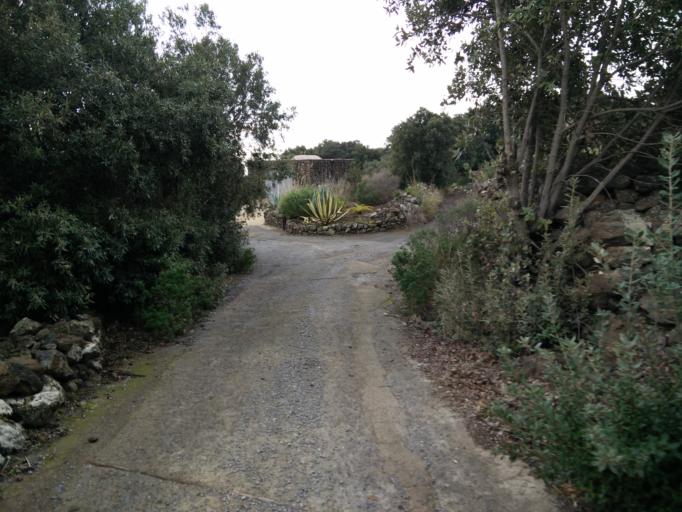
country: IT
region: Sicily
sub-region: Trapani
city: Kamma
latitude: 36.7494
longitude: 11.9964
